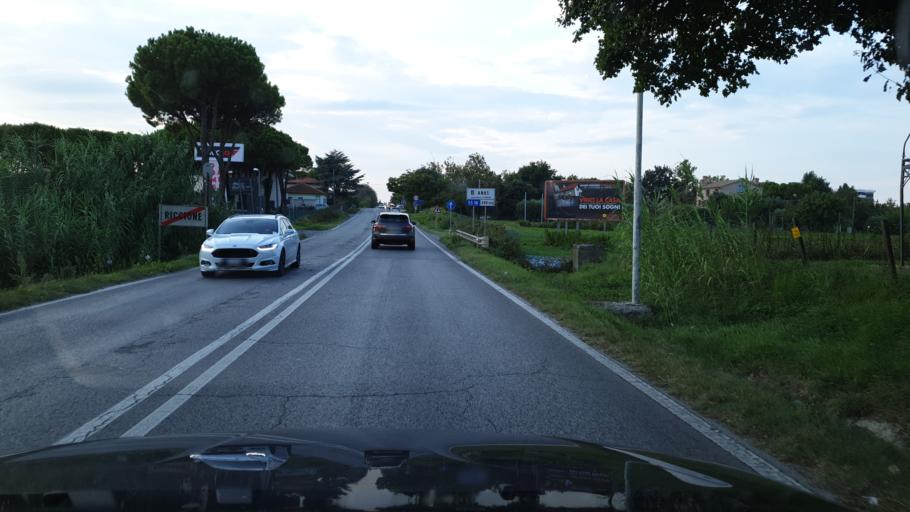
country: IT
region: Emilia-Romagna
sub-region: Provincia di Rimini
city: Rivazzurra
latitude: 44.0198
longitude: 12.6256
